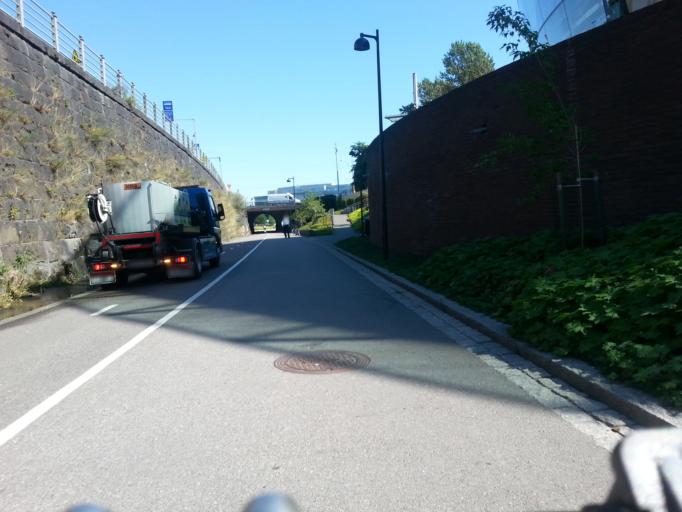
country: FI
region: Uusimaa
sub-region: Helsinki
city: Helsinki
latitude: 60.1714
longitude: 24.9336
